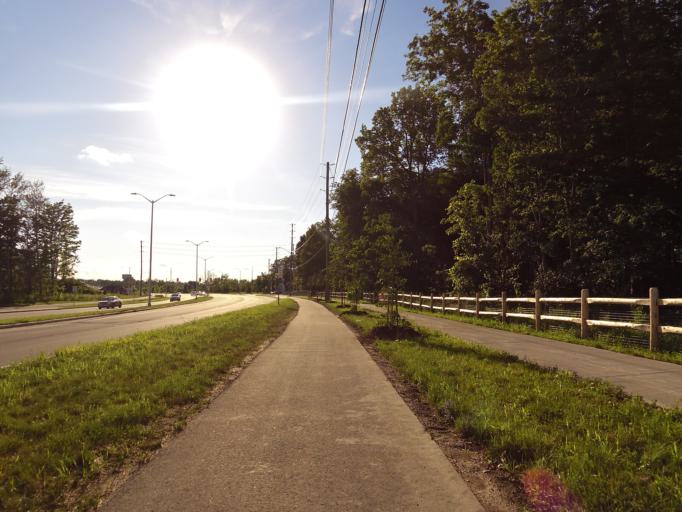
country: CA
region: Ontario
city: Bells Corners
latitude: 45.2722
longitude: -75.7847
